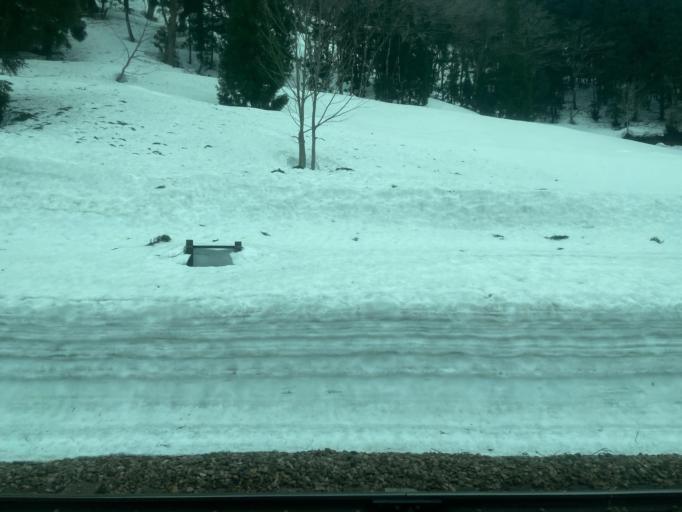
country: JP
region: Niigata
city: Shiozawa
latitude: 36.9328
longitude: 138.8154
